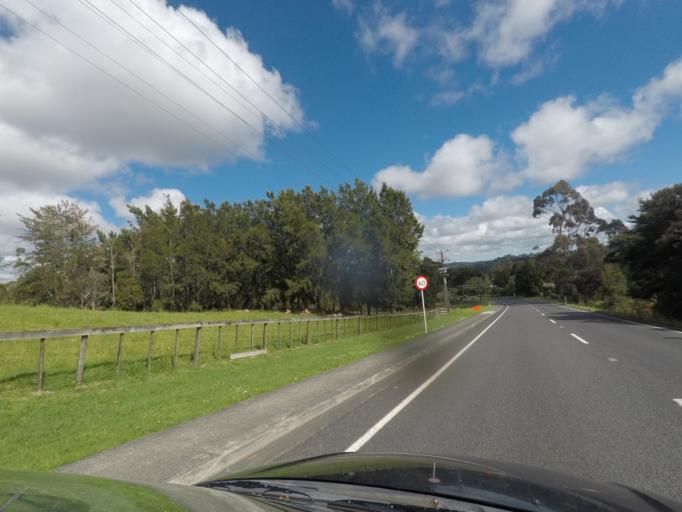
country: NZ
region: Auckland
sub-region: Auckland
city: Rothesay Bay
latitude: -36.7601
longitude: 174.6558
